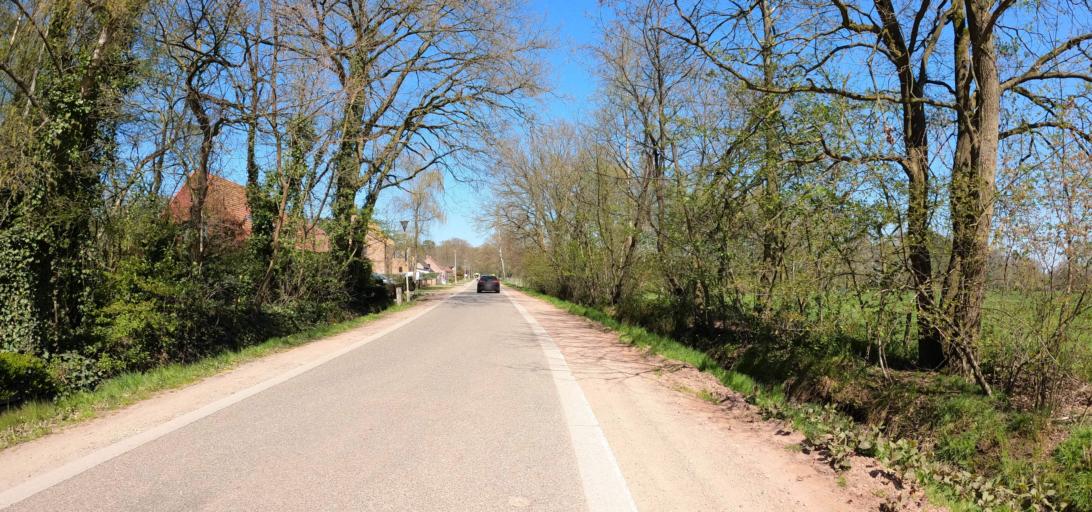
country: BE
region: Flanders
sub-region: Provincie Antwerpen
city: Oostmalle
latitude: 51.3046
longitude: 4.7524
